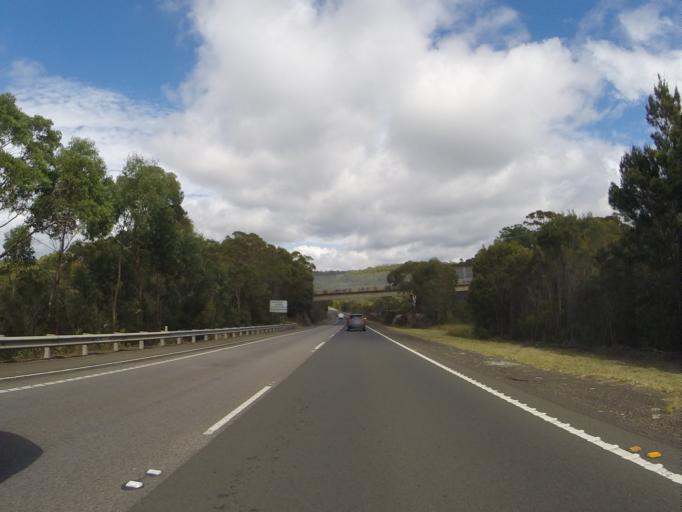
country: AU
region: New South Wales
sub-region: Wollongong
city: Helensburgh
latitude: -34.1587
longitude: 150.9839
